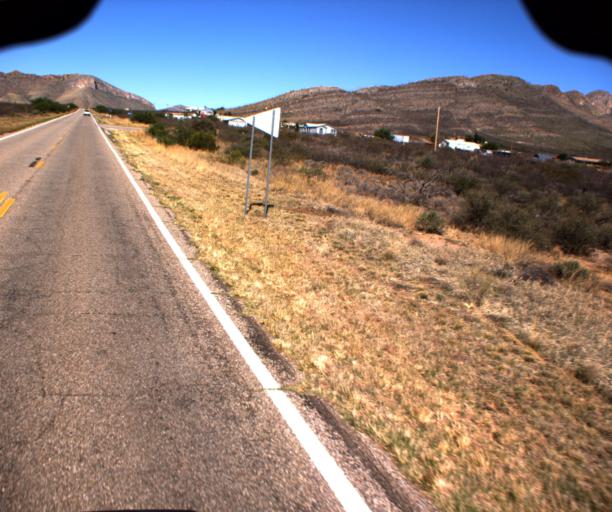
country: US
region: Arizona
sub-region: Cochise County
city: Huachuca City
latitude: 31.6921
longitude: -110.3810
